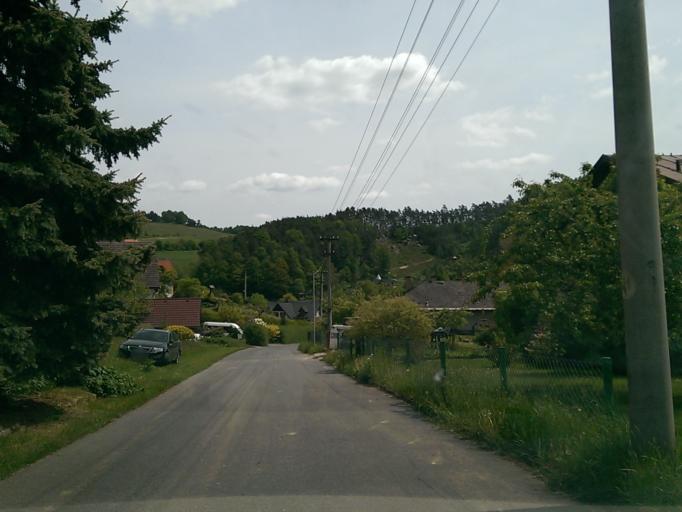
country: CZ
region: Liberecky
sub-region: Okres Semily
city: Turnov
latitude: 50.5496
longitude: 15.1393
